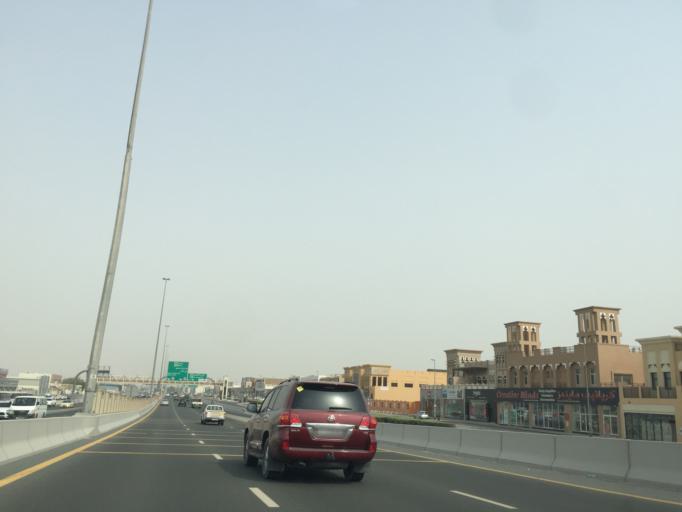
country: AE
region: Dubai
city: Dubai
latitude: 25.1156
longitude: 55.2128
